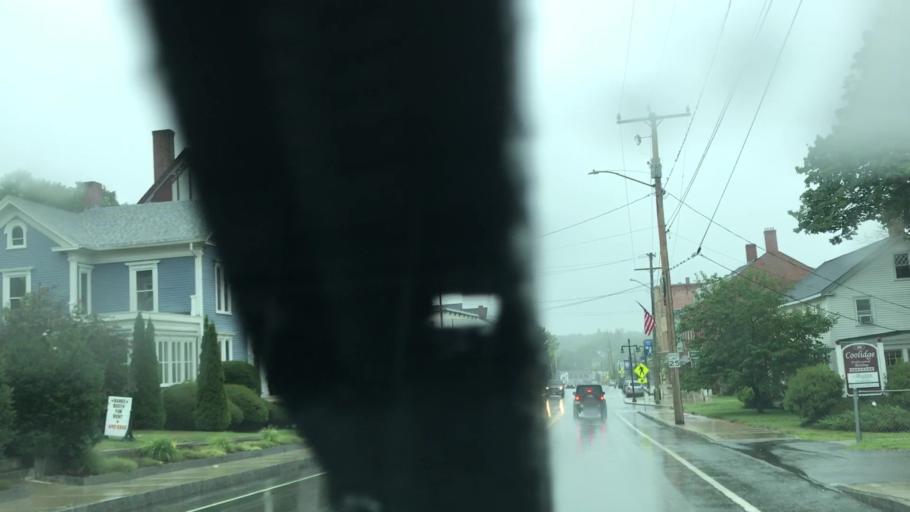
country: US
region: New Hampshire
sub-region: Strafford County
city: Somersworth
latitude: 43.2612
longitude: -70.8657
